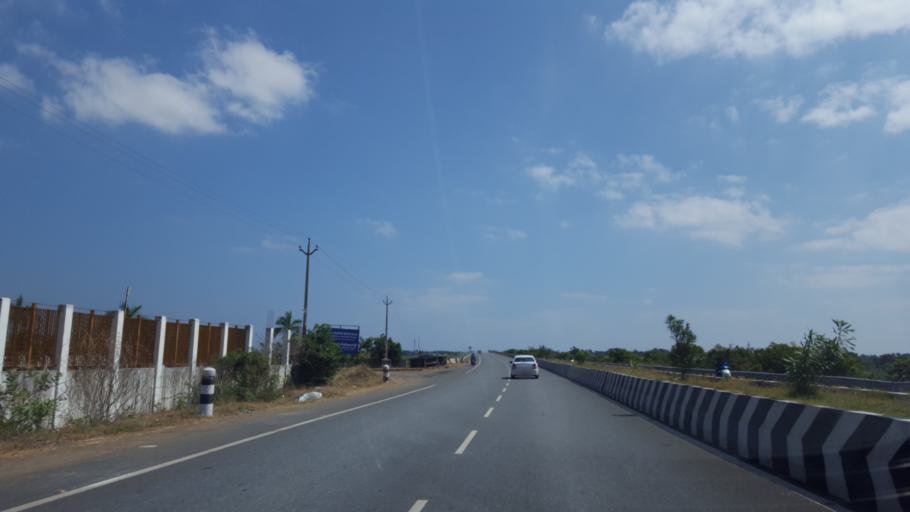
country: IN
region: Tamil Nadu
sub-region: Kancheepuram
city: Mamallapuram
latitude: 12.6196
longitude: 80.1813
